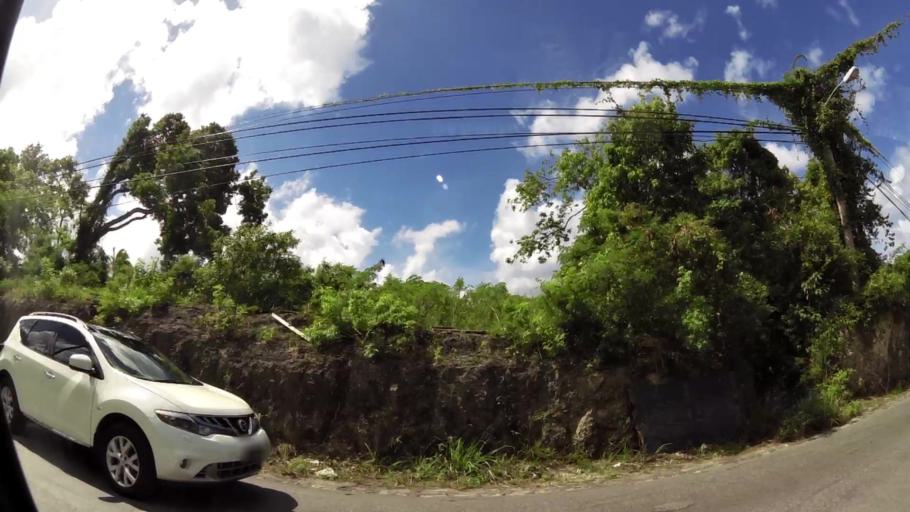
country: BB
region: Saint Michael
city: Bridgetown
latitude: 13.1365
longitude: -59.6351
